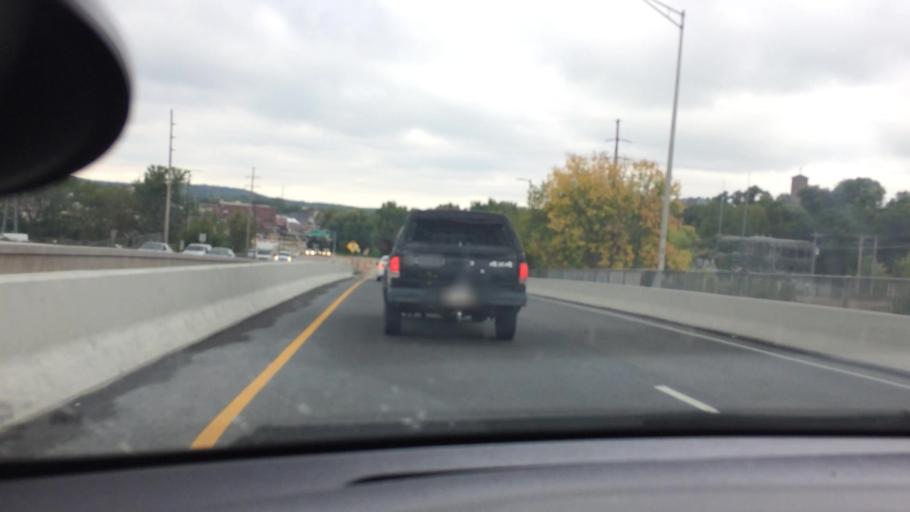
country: US
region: Wisconsin
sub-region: Chippewa County
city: Chippewa Falls
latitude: 44.9317
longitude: -91.3874
